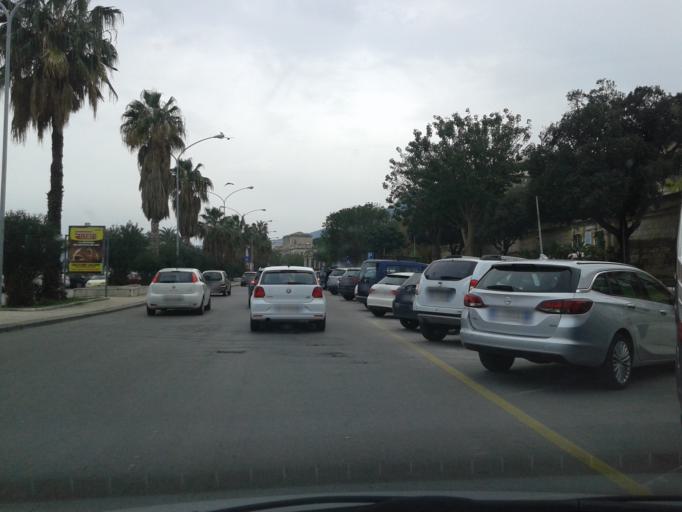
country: IT
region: Sicily
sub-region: Palermo
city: Palermo
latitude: 38.1196
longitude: 13.3716
